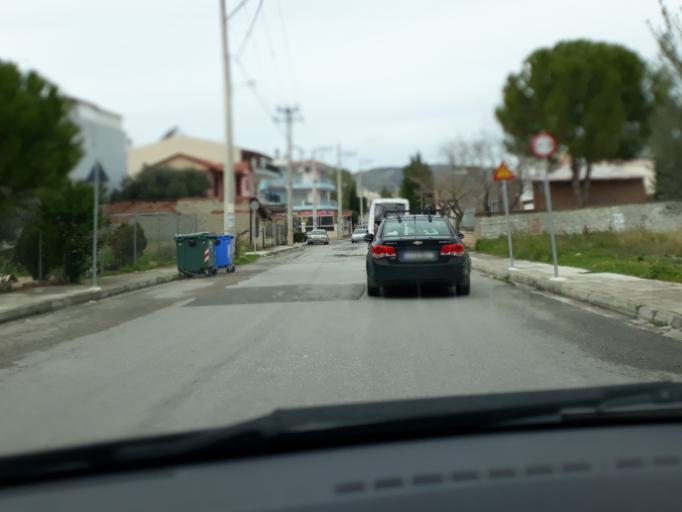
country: GR
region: Attica
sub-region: Nomarchia Dytikis Attikis
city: Ano Liosia
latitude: 38.0902
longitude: 23.7131
